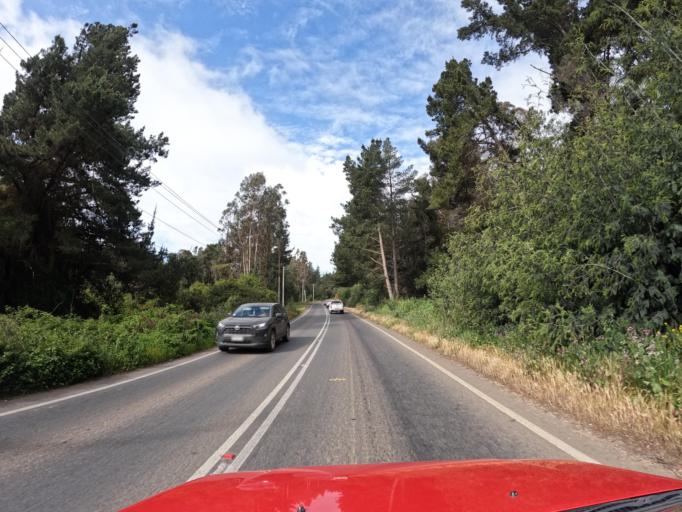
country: CL
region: O'Higgins
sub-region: Provincia de Colchagua
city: Santa Cruz
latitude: -34.3548
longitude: -71.9111
